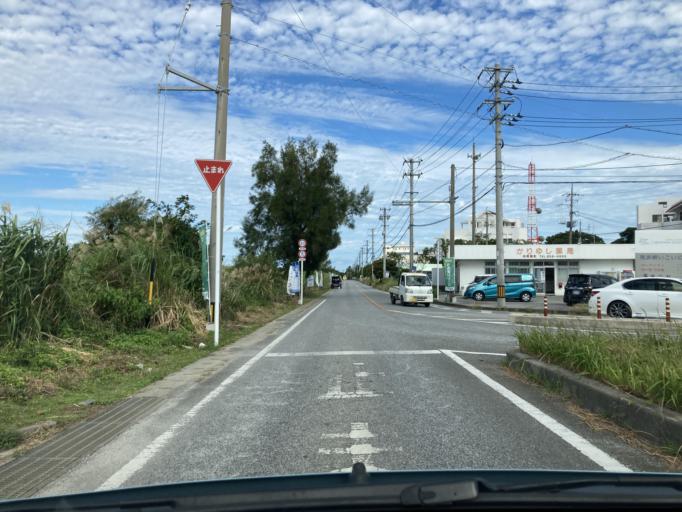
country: JP
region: Okinawa
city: Ishikawa
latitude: 26.4241
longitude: 127.7304
